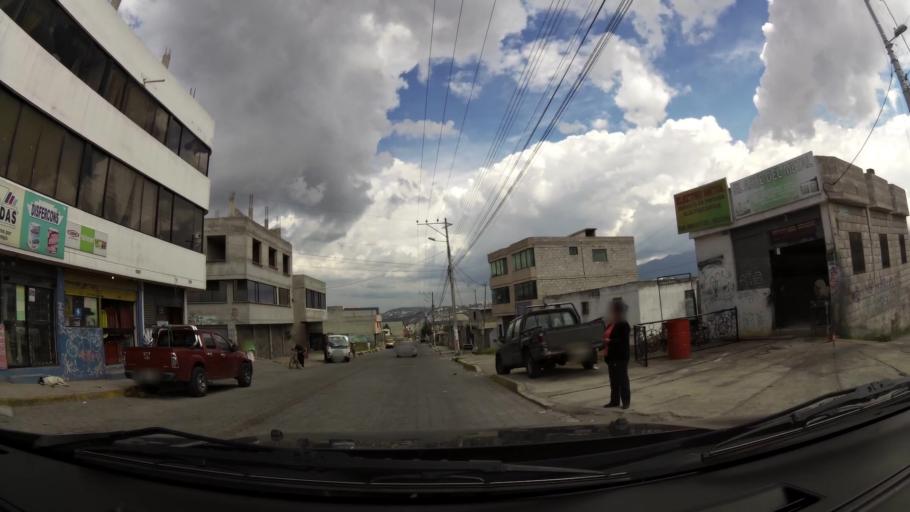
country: EC
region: Pichincha
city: Quito
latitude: -0.0791
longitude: -78.4359
